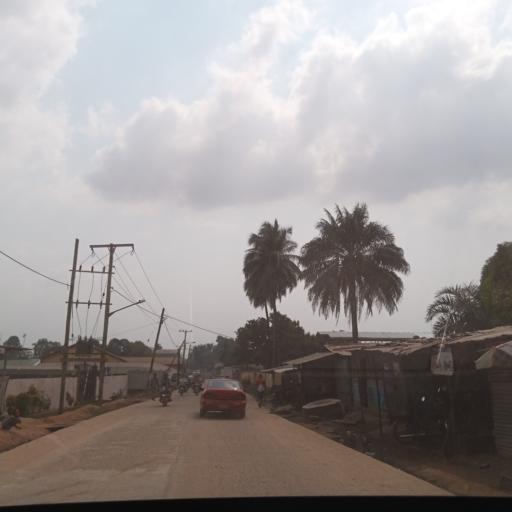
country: LR
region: Montserrado
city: Monrovia
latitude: 6.2860
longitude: -10.6900
